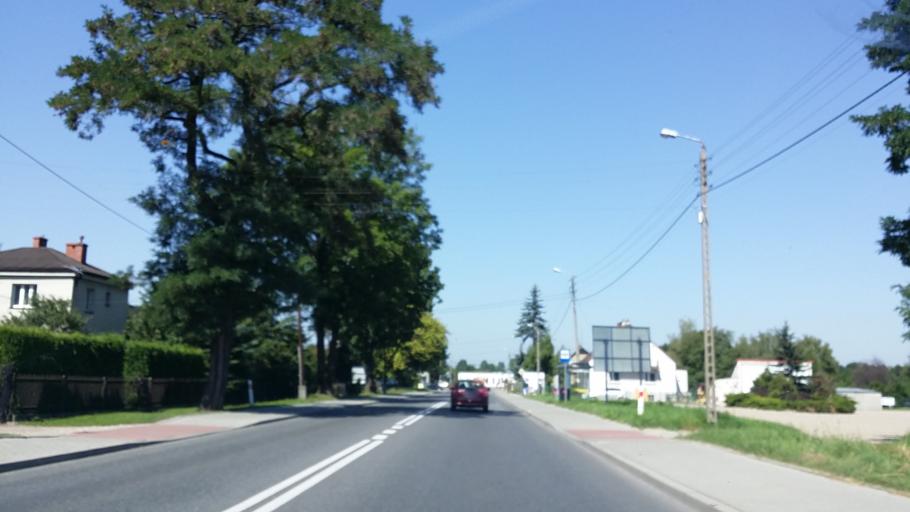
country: PL
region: Lesser Poland Voivodeship
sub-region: Powiat wadowicki
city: Tomice
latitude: 49.8928
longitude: 19.4897
